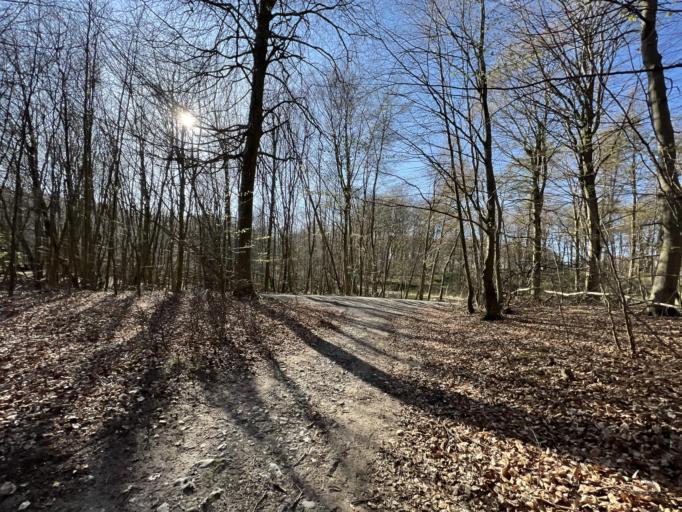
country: DE
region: Mecklenburg-Vorpommern
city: Sassnitz
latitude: 54.5402
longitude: 13.6280
